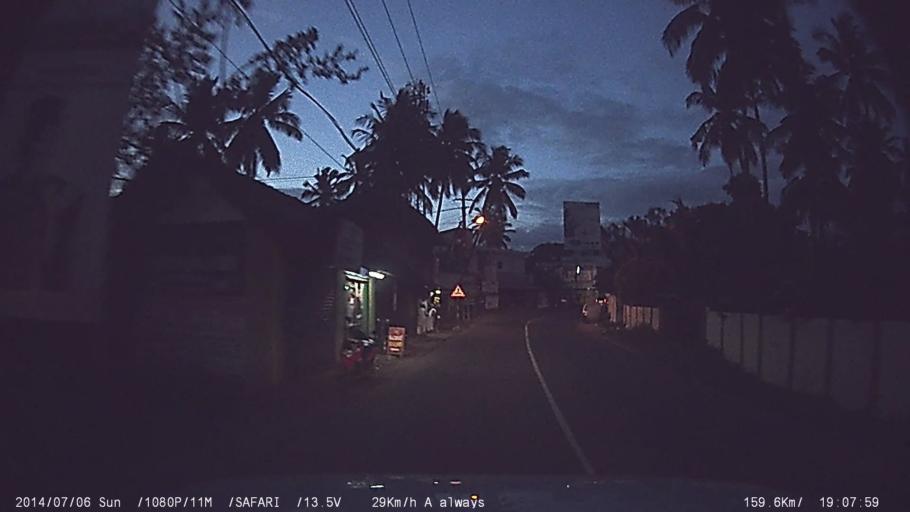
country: IN
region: Kerala
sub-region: Palakkad district
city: Palakkad
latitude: 10.7510
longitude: 76.6497
